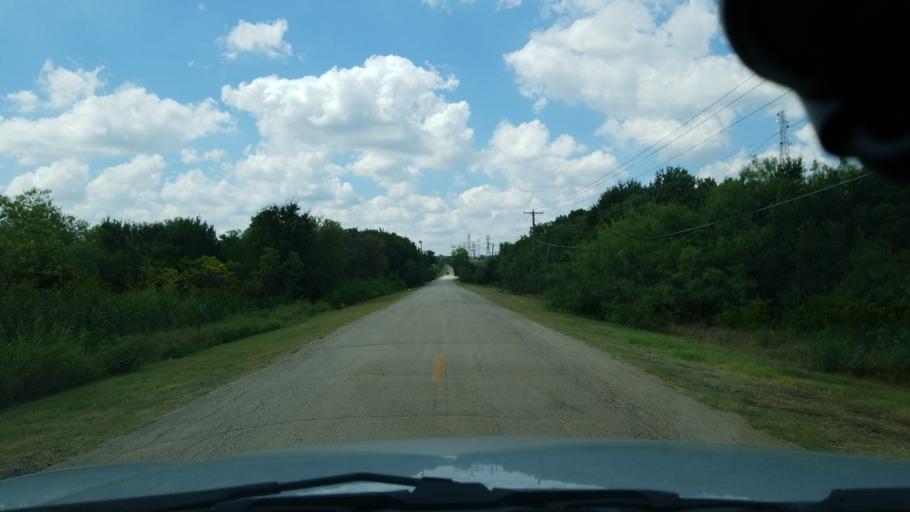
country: US
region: Texas
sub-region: Dallas County
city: Cockrell Hill
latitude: 32.7280
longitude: -96.9309
